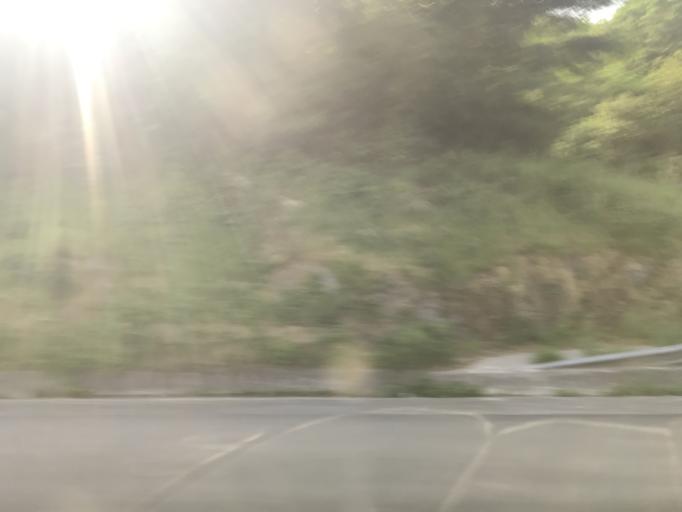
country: ES
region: Basque Country
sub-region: Provincia de Guipuzcoa
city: Aduna
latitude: 43.1993
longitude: -2.0396
